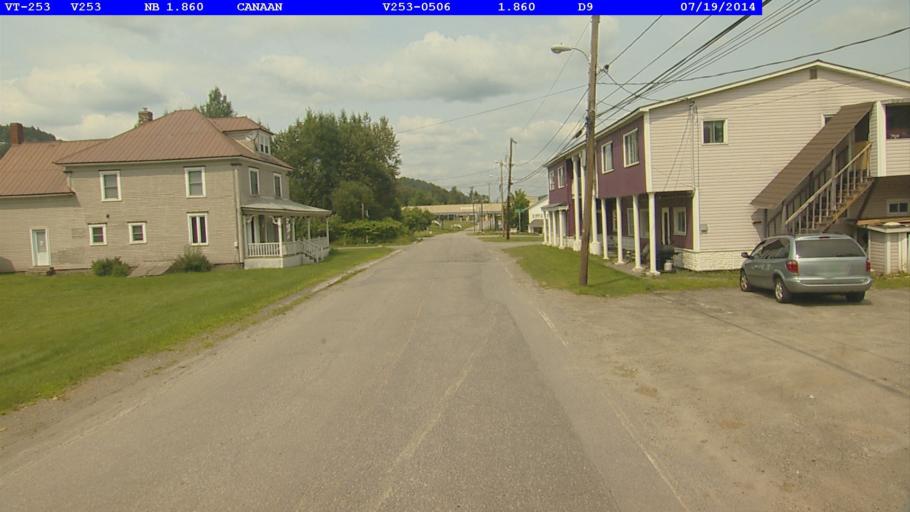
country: US
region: New Hampshire
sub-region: Coos County
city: Colebrook
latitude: 45.0092
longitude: -71.5070
